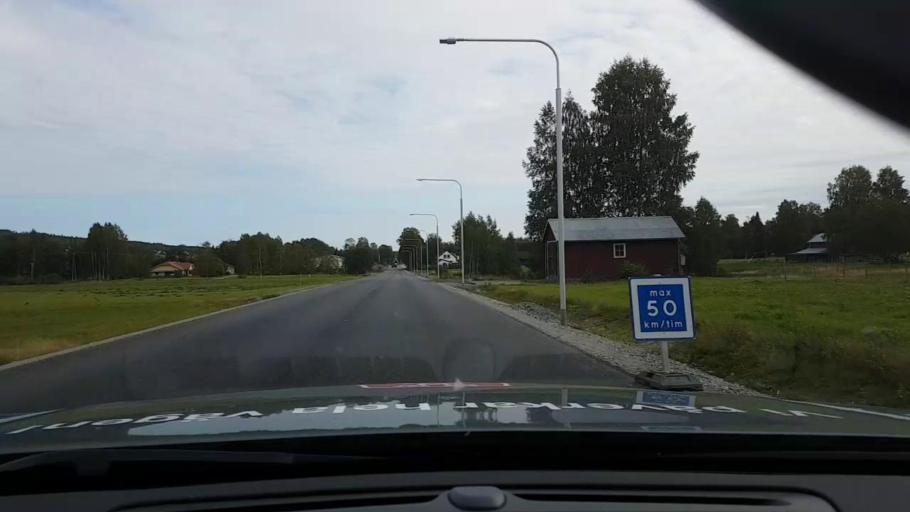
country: SE
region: Vaesternorrland
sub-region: OErnskoeldsviks Kommun
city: Bjasta
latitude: 63.2894
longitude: 18.4348
